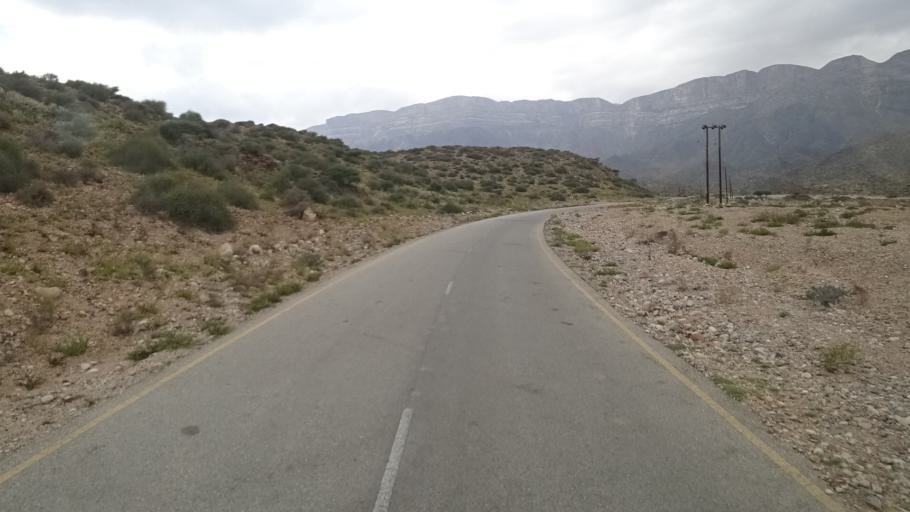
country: OM
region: Zufar
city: Salalah
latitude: 17.1688
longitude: 54.9750
